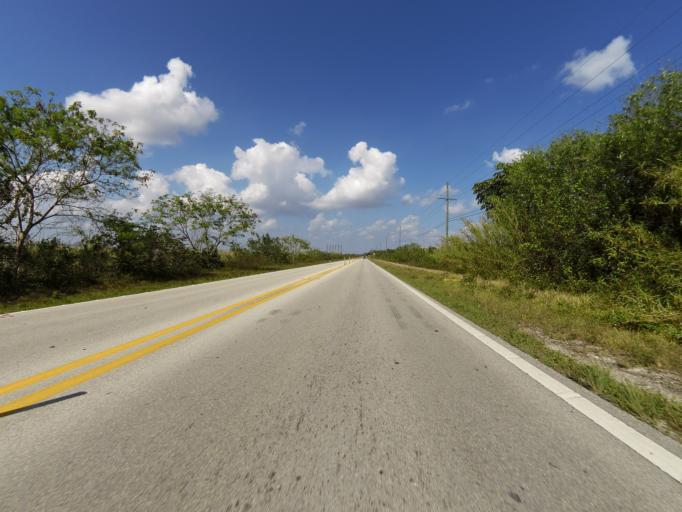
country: US
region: Florida
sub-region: Miami-Dade County
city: Palm Springs North
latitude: 25.9369
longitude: -80.4437
